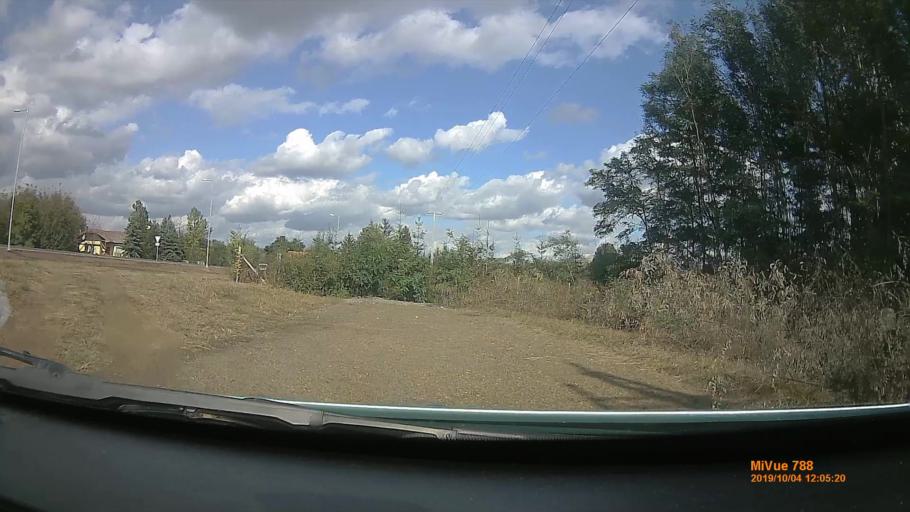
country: HU
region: Szabolcs-Szatmar-Bereg
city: Kotaj
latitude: 48.0222
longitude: 21.6801
